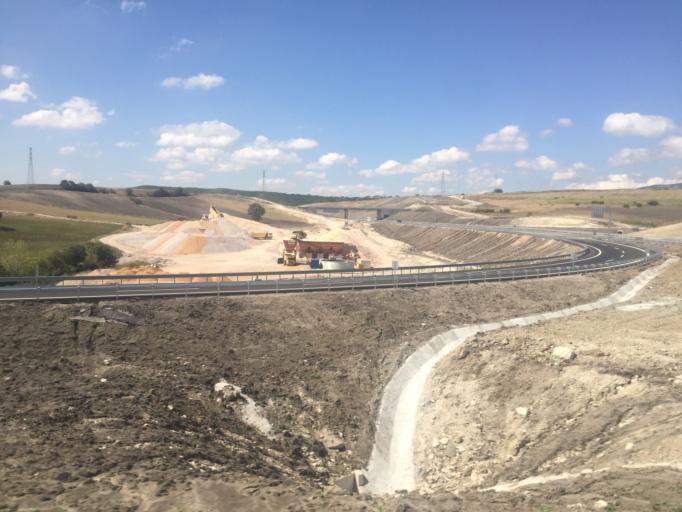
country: TR
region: Balikesir
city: Gobel
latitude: 39.9683
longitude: 28.1627
